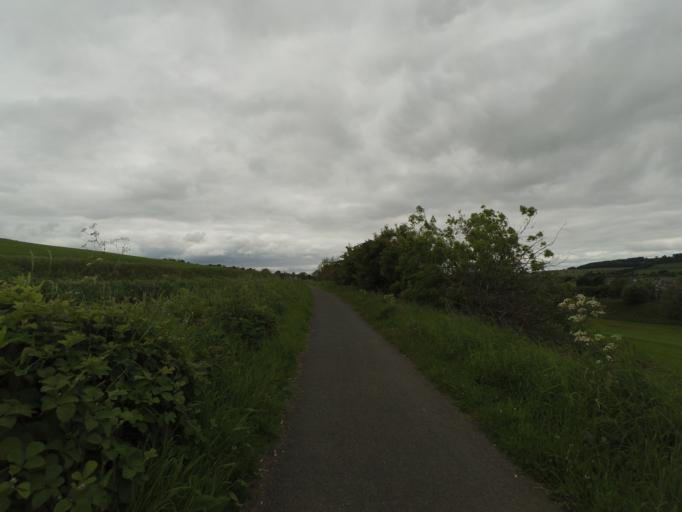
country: GB
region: Scotland
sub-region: West Lothian
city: Linlithgow
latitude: 55.9772
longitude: -3.5787
